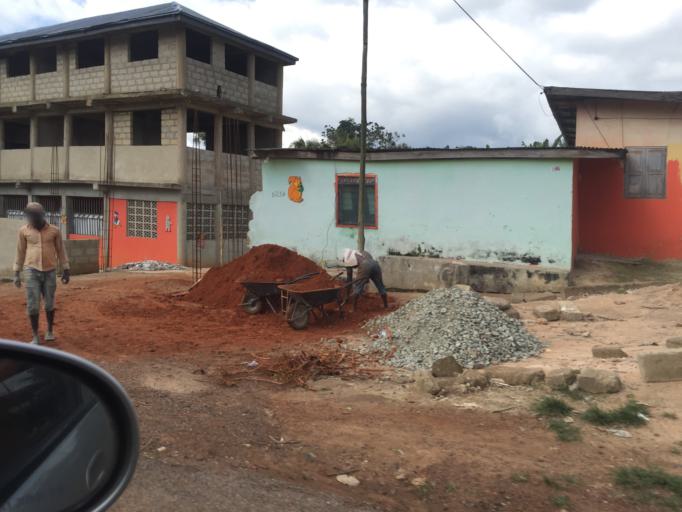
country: GH
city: Mpraeso
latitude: 6.5976
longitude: -0.7388
